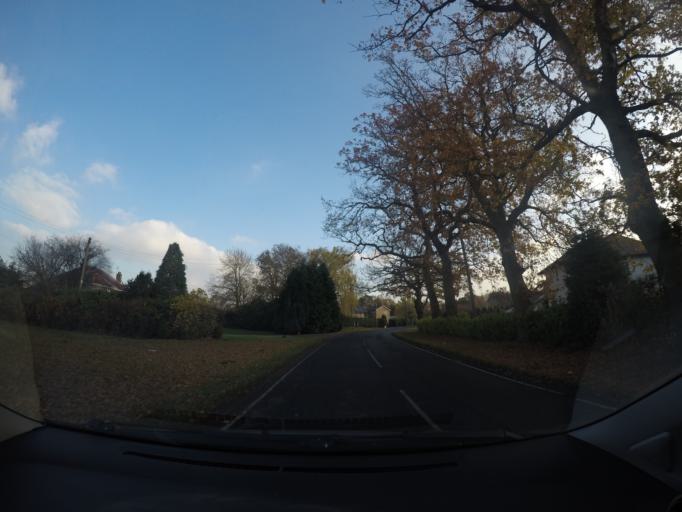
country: GB
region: England
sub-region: City of York
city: Huntington
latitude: 53.9994
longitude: -1.0204
